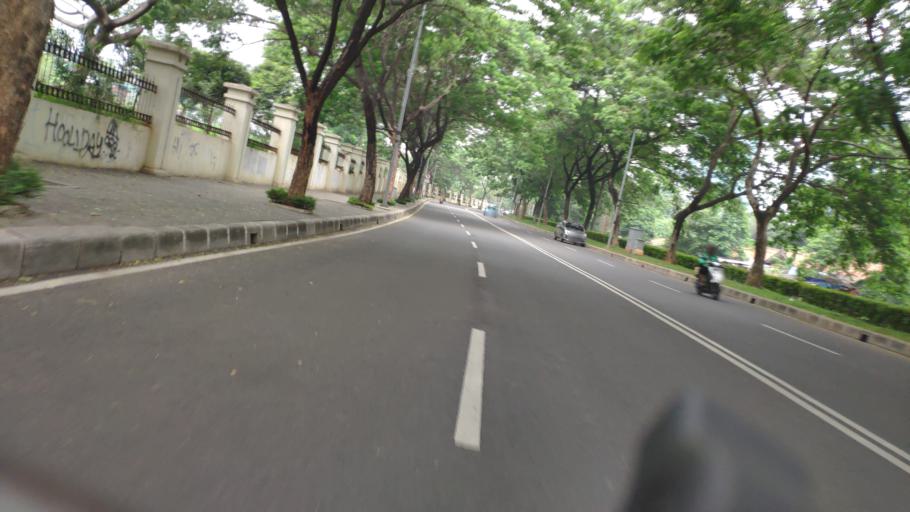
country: ID
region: Jakarta Raya
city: Jakarta
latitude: -6.2225
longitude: 106.8360
